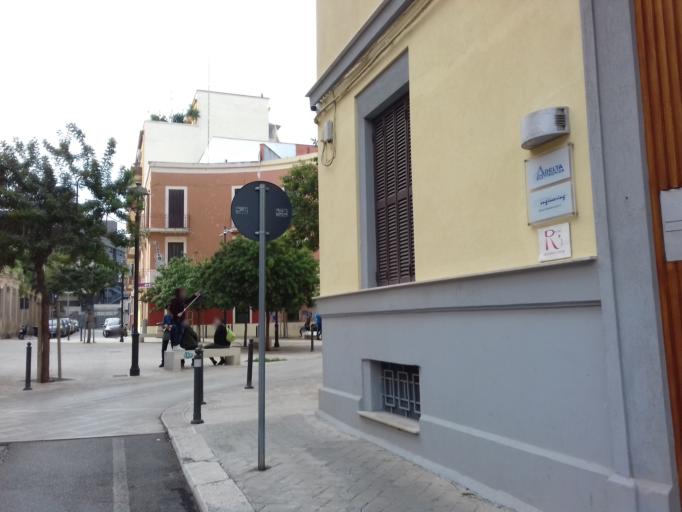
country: IT
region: Apulia
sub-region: Provincia di Bari
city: Bari
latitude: 41.1138
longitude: 16.8783
